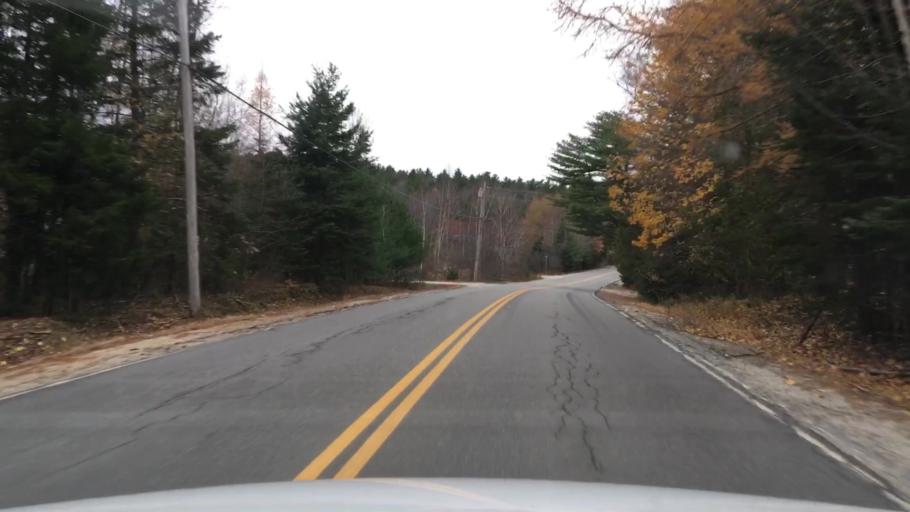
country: US
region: Maine
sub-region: Hancock County
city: Penobscot
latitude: 44.4221
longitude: -68.6208
